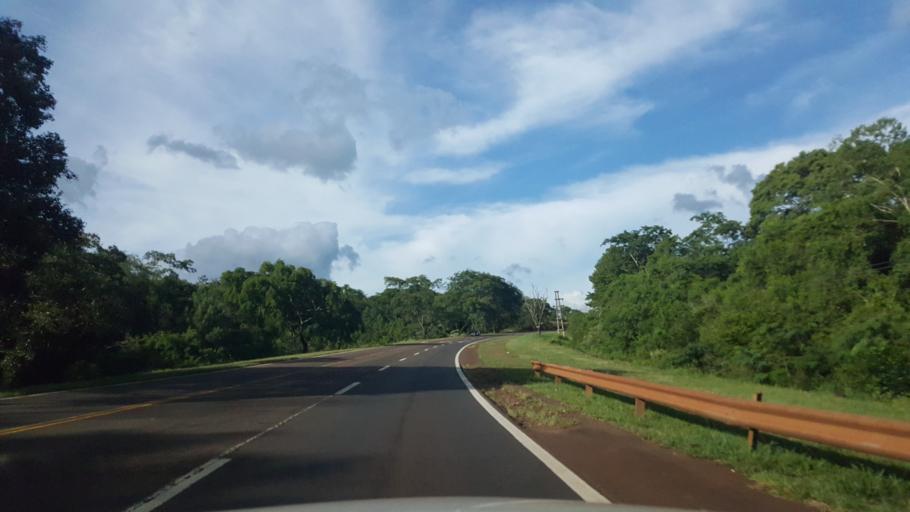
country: AR
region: Misiones
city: Santa Ana
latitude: -27.3591
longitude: -55.5570
